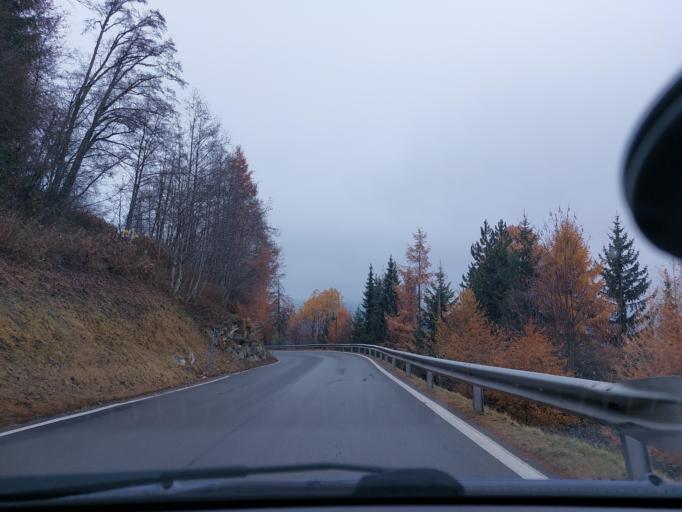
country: CH
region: Valais
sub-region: Conthey District
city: Basse-Nendaz
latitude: 46.1799
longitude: 7.3106
